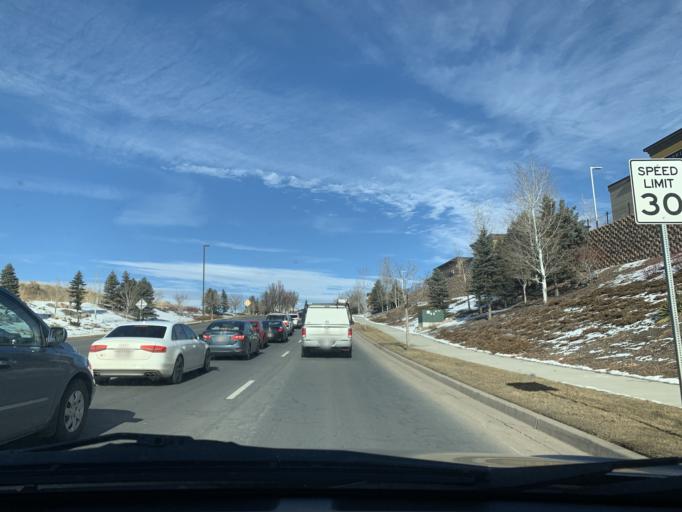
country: US
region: Utah
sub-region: Utah County
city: Lehi
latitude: 40.4325
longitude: -111.8809
